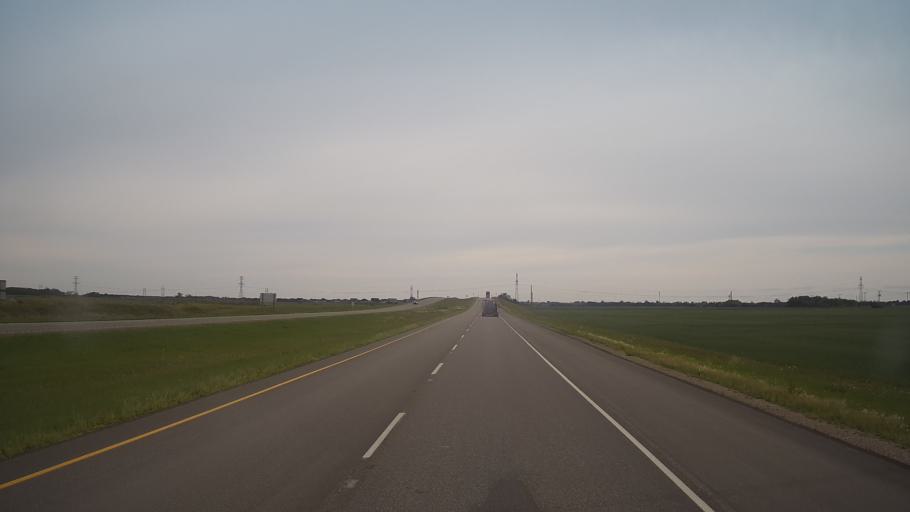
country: CA
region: Saskatchewan
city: Saskatoon
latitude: 52.0638
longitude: -106.6014
